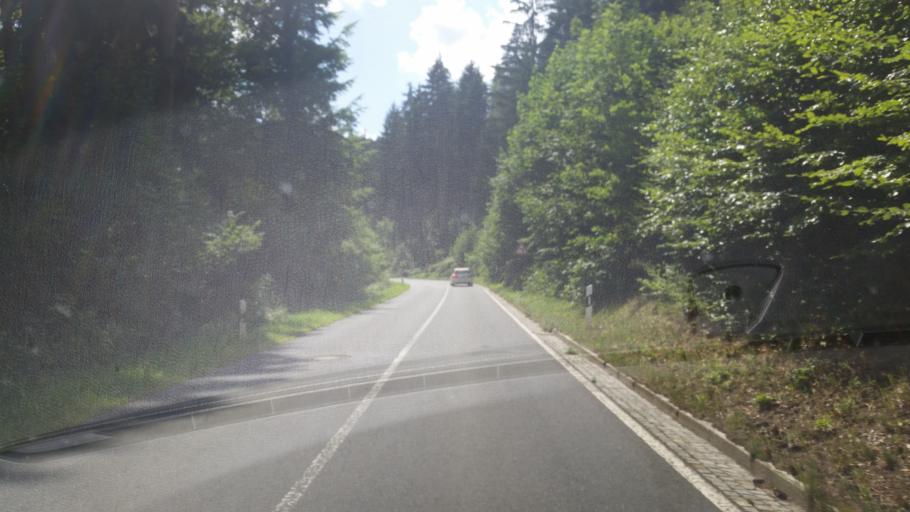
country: DE
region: Saxony
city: Glashutte
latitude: 50.8429
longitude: 13.7322
